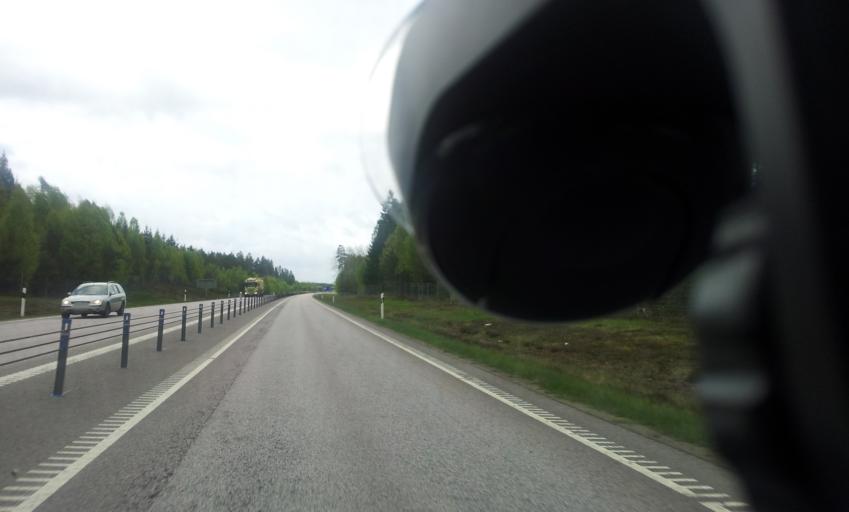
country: SE
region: Kalmar
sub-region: Torsas Kommun
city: Torsas
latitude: 56.5119
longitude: 16.0863
